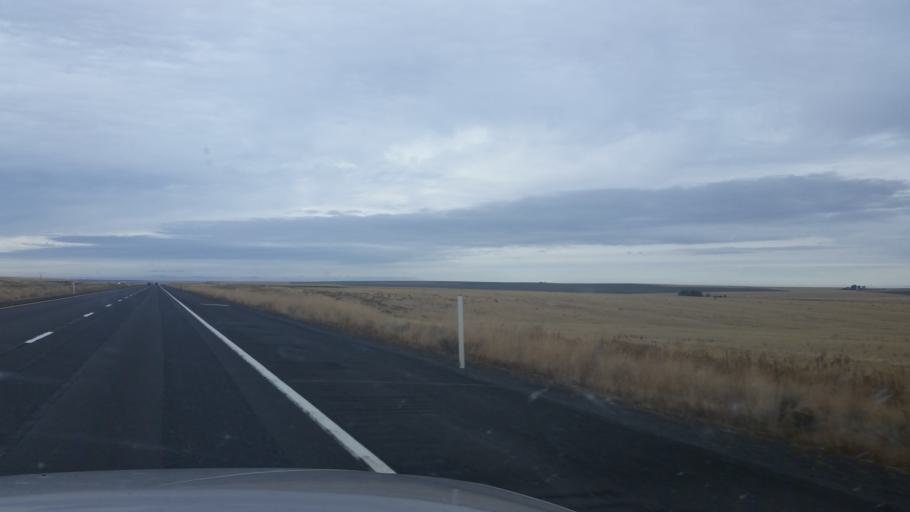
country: US
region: Washington
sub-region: Adams County
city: Ritzville
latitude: 47.1111
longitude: -118.5092
